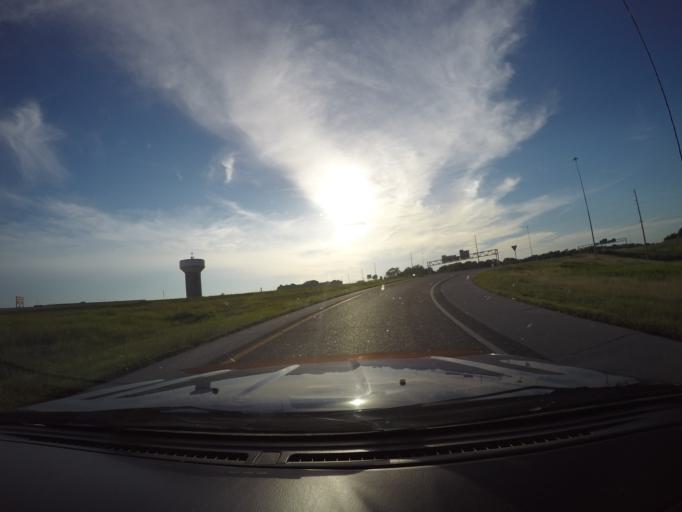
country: US
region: Kansas
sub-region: Wyandotte County
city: Edwardsville
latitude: 39.1272
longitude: -94.8152
